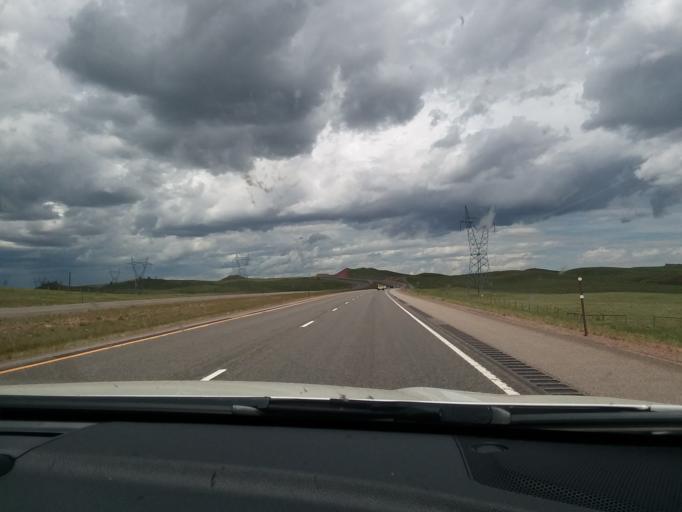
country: US
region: Wyoming
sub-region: Albany County
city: Laramie
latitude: 41.0355
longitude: -105.4431
